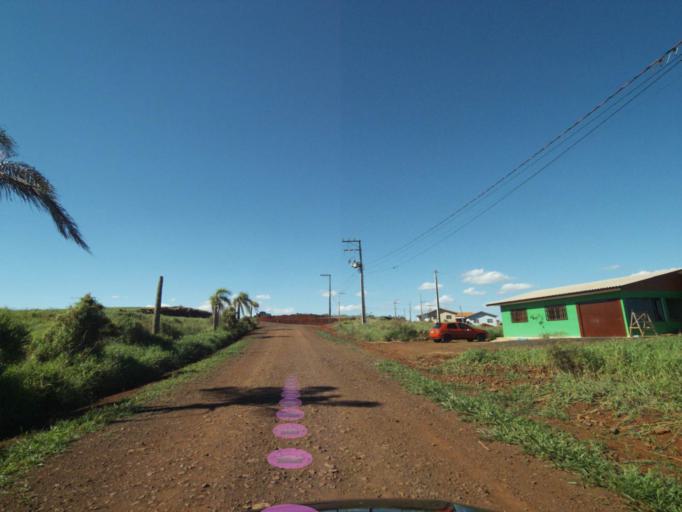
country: BR
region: Parana
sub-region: Coronel Vivida
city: Coronel Vivida
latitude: -26.1377
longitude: -52.3935
